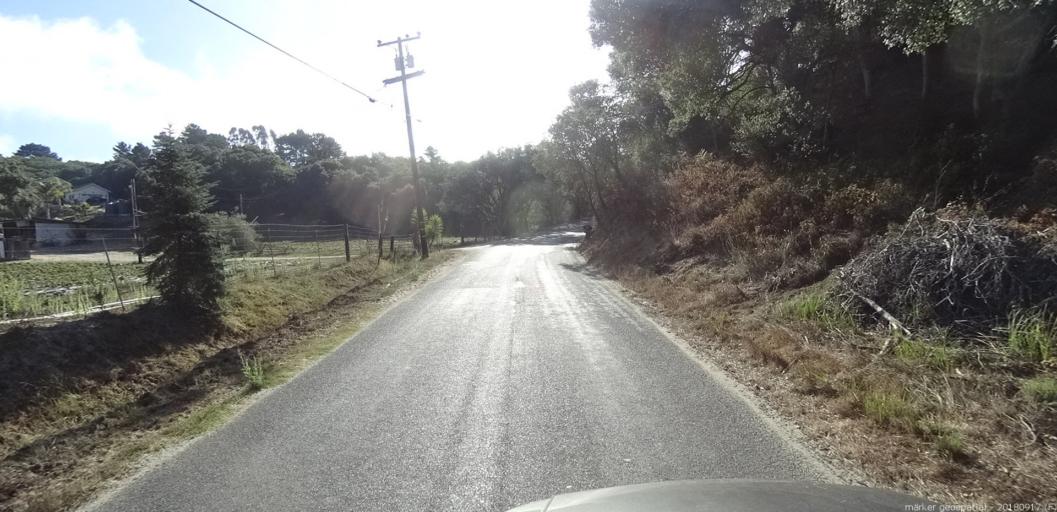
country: US
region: California
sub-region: Monterey County
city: Elkhorn
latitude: 36.8126
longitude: -121.7162
